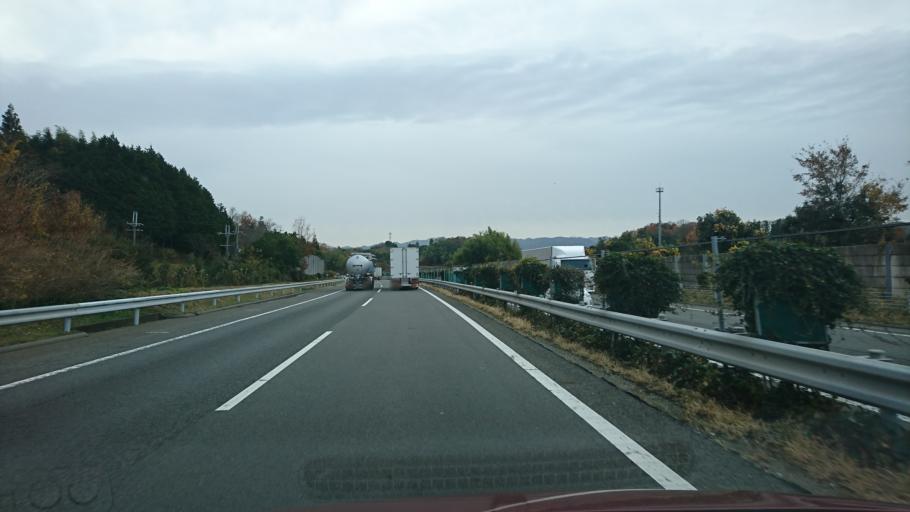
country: JP
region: Hyogo
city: Sandacho
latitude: 34.8279
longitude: 135.1723
